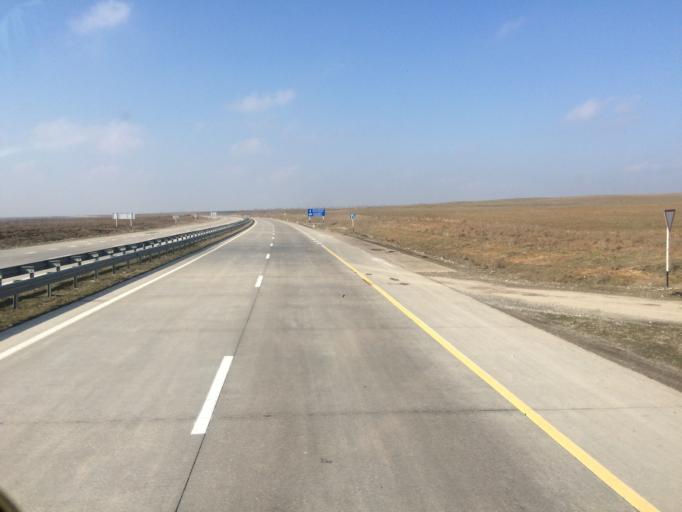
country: KZ
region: Ongtustik Qazaqstan
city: Shymkent
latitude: 42.4883
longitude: 69.5184
